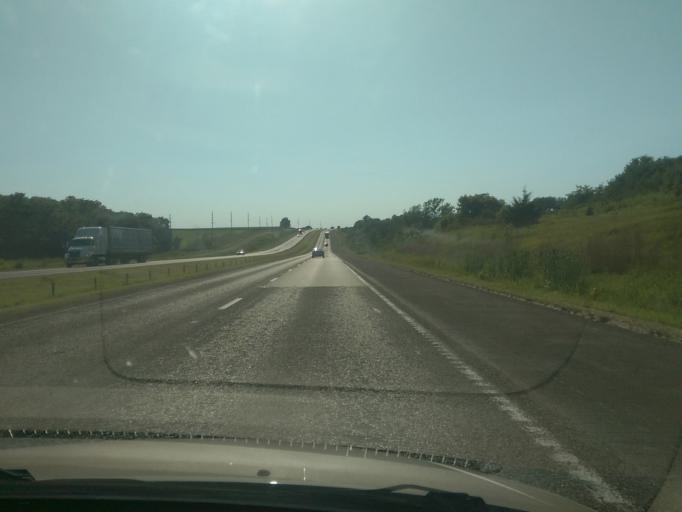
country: US
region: Missouri
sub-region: Lafayette County
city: Higginsville
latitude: 38.9928
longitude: -93.6979
